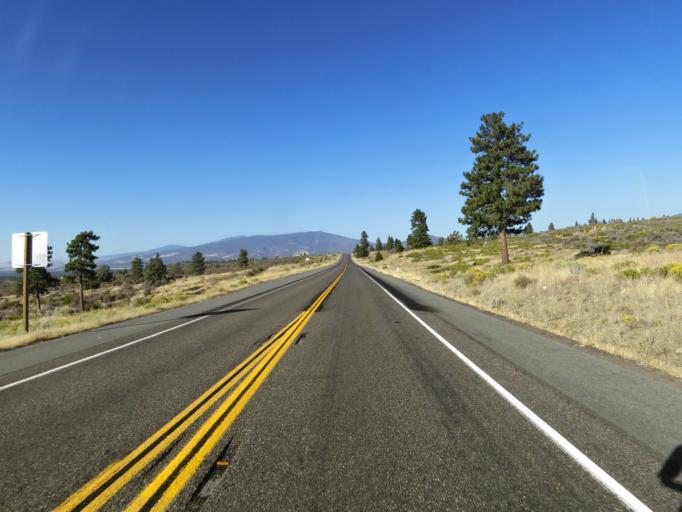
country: US
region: California
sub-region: Siskiyou County
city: Weed
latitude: 41.4866
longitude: -122.3391
